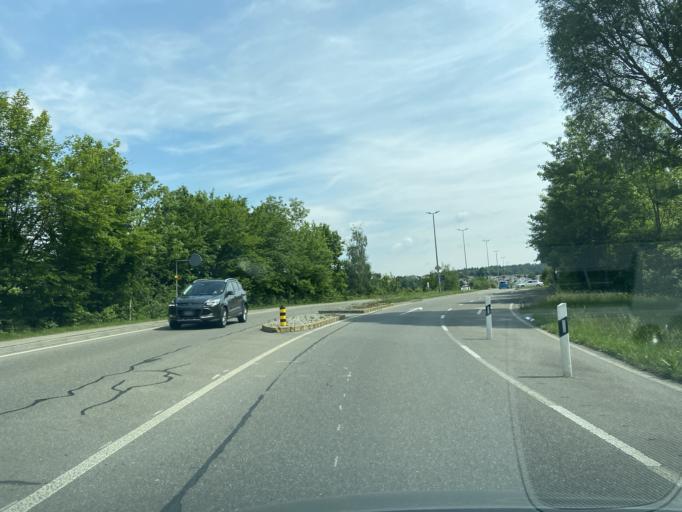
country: CH
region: Zurich
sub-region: Bezirk Uster
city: Duebendorf / Kunklerstrasse
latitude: 47.4101
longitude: 8.6333
